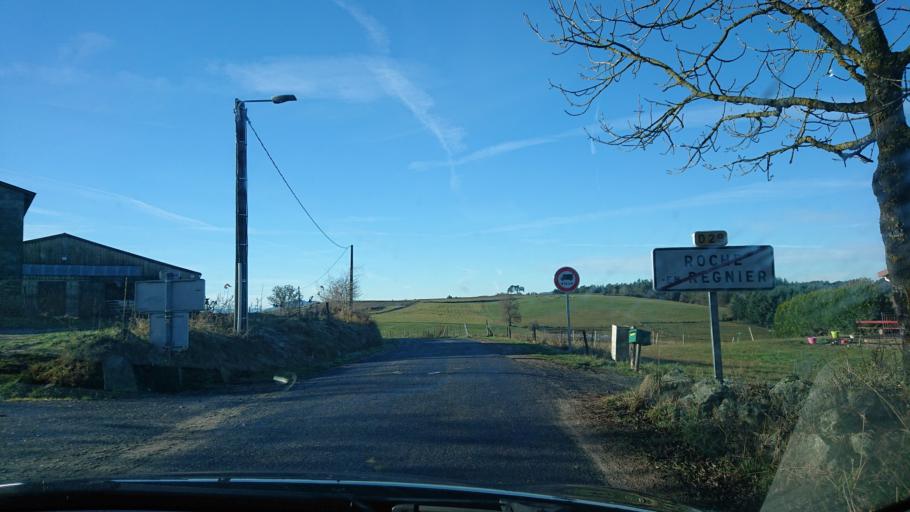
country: FR
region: Auvergne
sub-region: Departement de la Haute-Loire
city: Vorey
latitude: 45.2197
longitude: 3.9394
